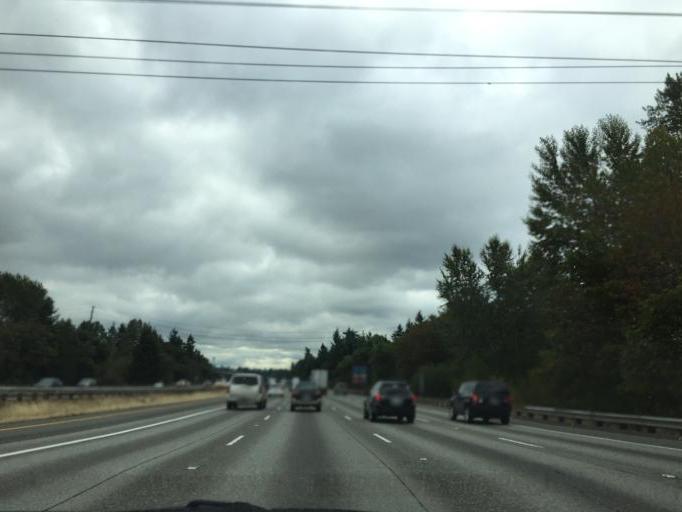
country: US
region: Washington
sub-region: King County
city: Des Moines
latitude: 47.4037
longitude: -122.2927
